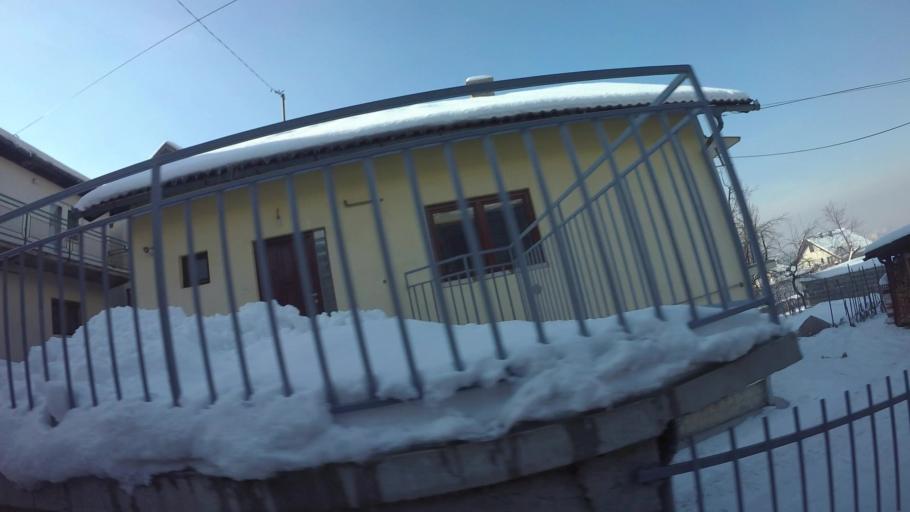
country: BA
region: Federation of Bosnia and Herzegovina
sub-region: Kanton Sarajevo
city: Sarajevo
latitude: 43.8402
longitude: 18.3634
